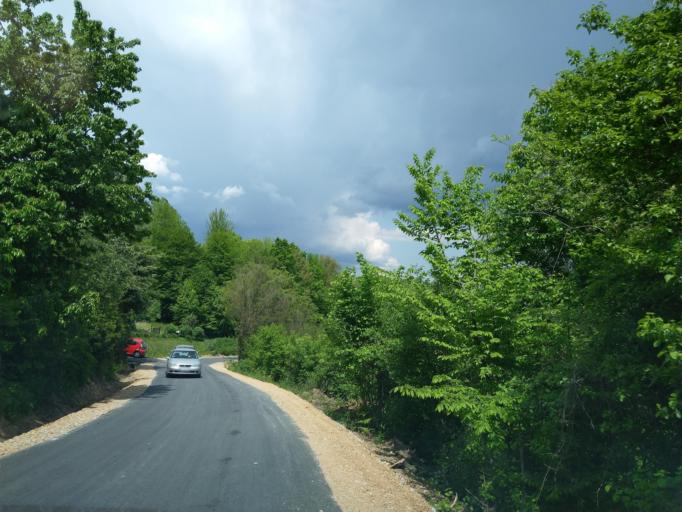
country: RS
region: Central Serbia
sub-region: Zlatiborski Okrug
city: Uzice
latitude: 43.8588
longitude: 19.9251
